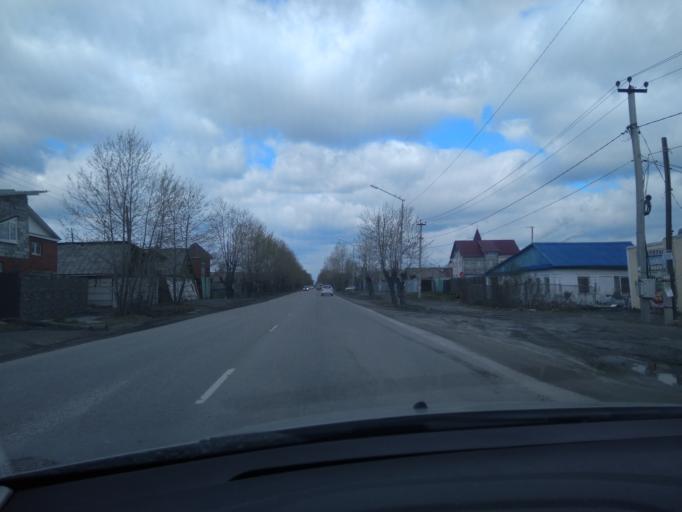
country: RU
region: Sverdlovsk
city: Sredneuralsk
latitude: 56.9897
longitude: 60.4919
